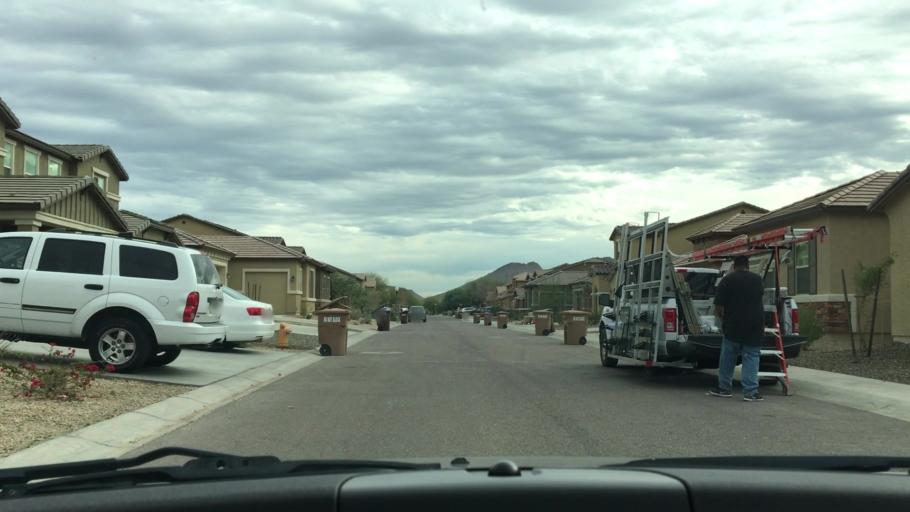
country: US
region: Arizona
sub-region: Maricopa County
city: Sun City West
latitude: 33.7264
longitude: -112.2310
